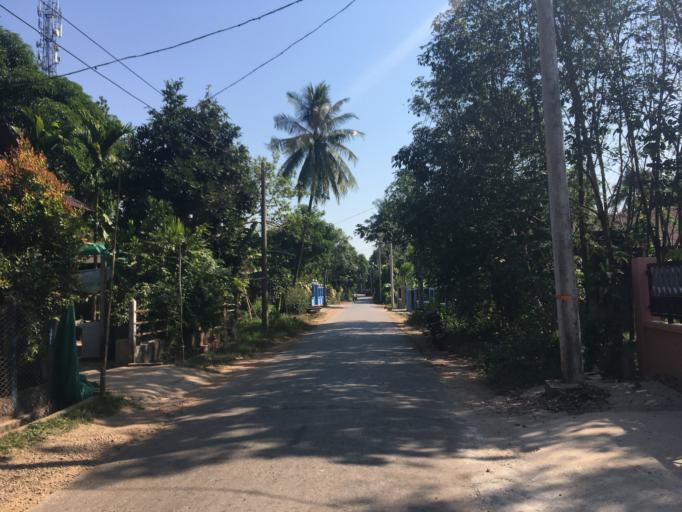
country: MM
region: Mon
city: Mawlamyine
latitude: 16.4321
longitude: 97.6989
